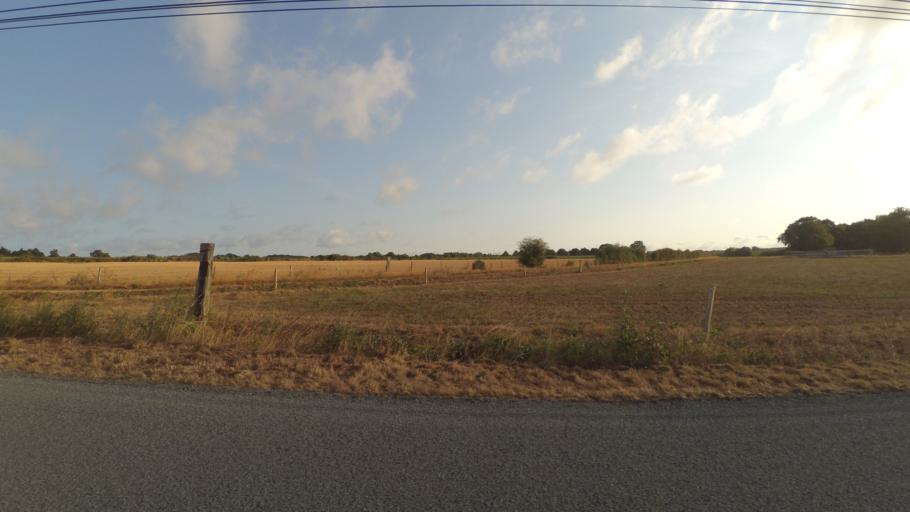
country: FR
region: Pays de la Loire
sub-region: Departement de la Loire-Atlantique
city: La Planche
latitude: 47.0184
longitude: -1.4187
